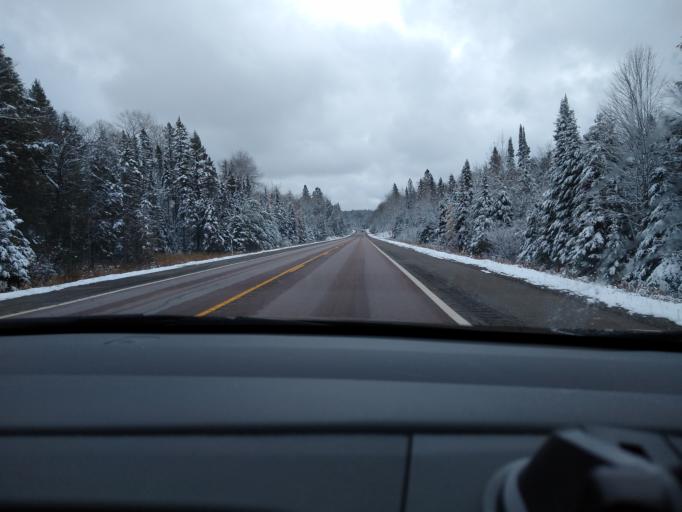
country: US
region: Wisconsin
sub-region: Vilas County
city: Eagle River
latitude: 46.2401
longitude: -89.0915
